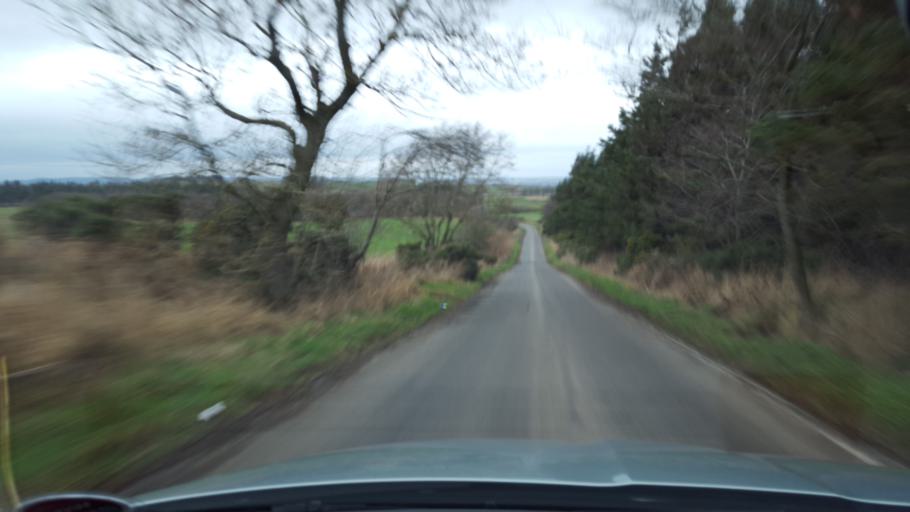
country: GB
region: Scotland
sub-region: West Lothian
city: Kirknewton
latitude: 55.8679
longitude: -3.4338
